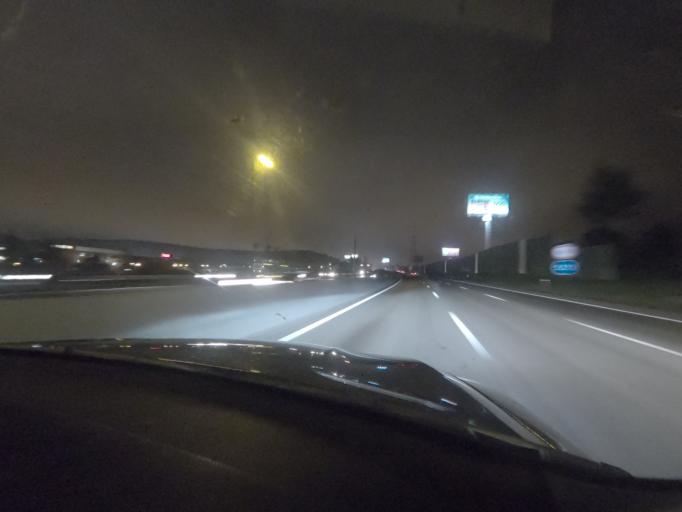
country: PT
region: Lisbon
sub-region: Vila Franca de Xira
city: Vialonga
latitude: 38.8849
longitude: -9.0588
